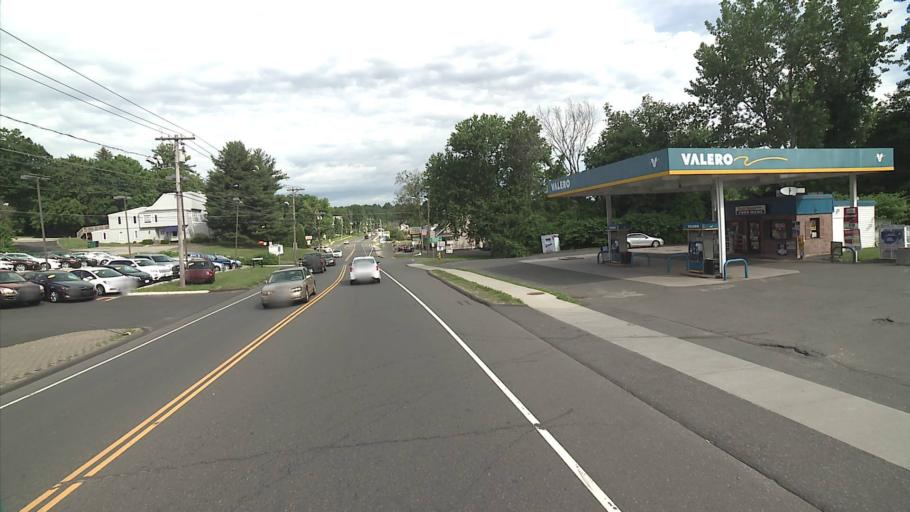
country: US
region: Connecticut
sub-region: Litchfield County
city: Watertown
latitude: 41.5920
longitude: -73.1076
